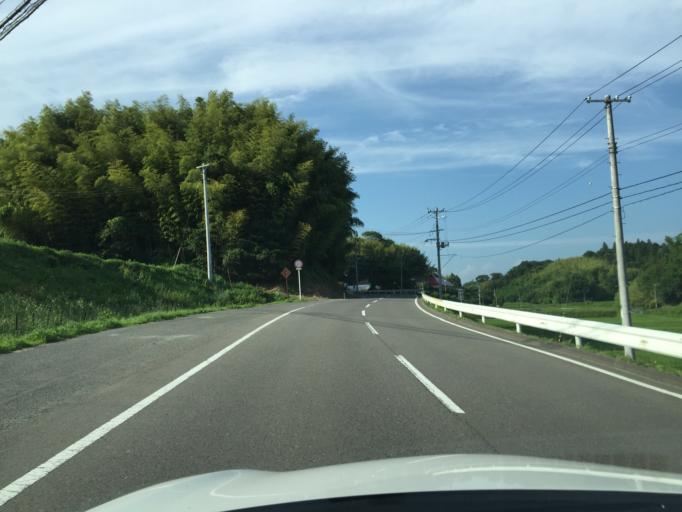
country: JP
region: Fukushima
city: Miharu
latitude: 37.4256
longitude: 140.5002
